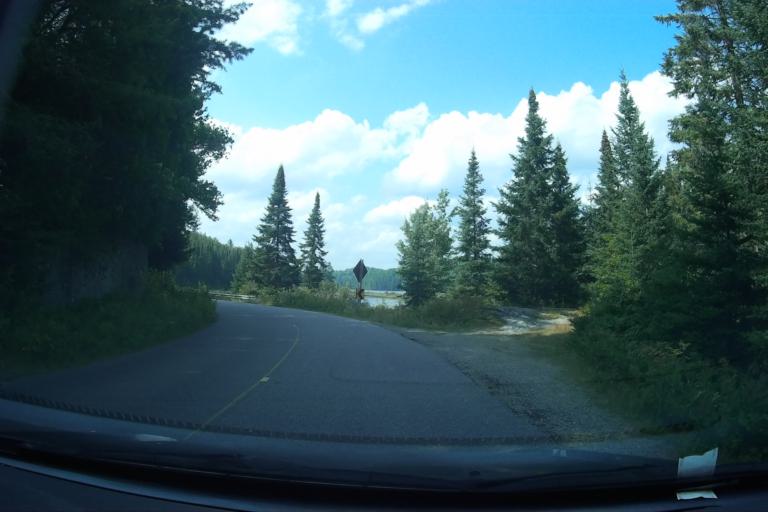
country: CA
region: Ontario
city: Bancroft
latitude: 45.6304
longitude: -78.3521
